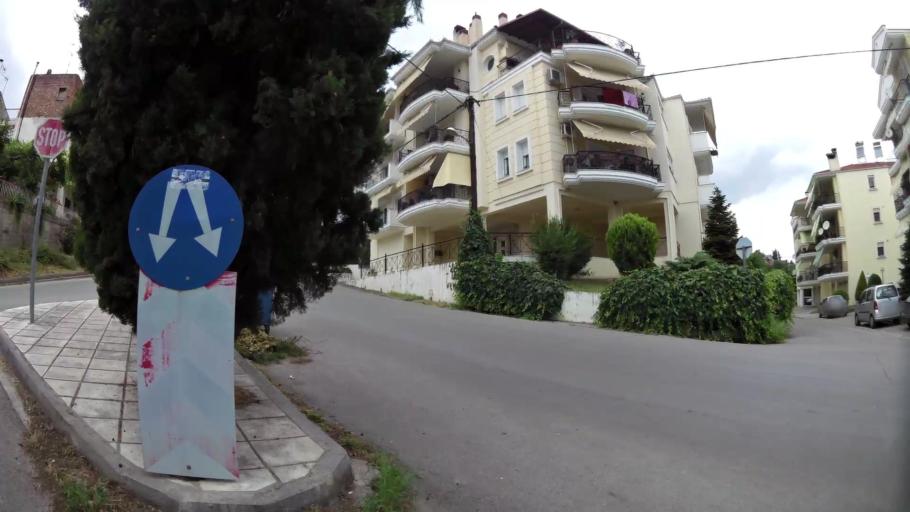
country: GR
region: Central Macedonia
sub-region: Nomos Imathias
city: Veroia
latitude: 40.5219
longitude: 22.2098
